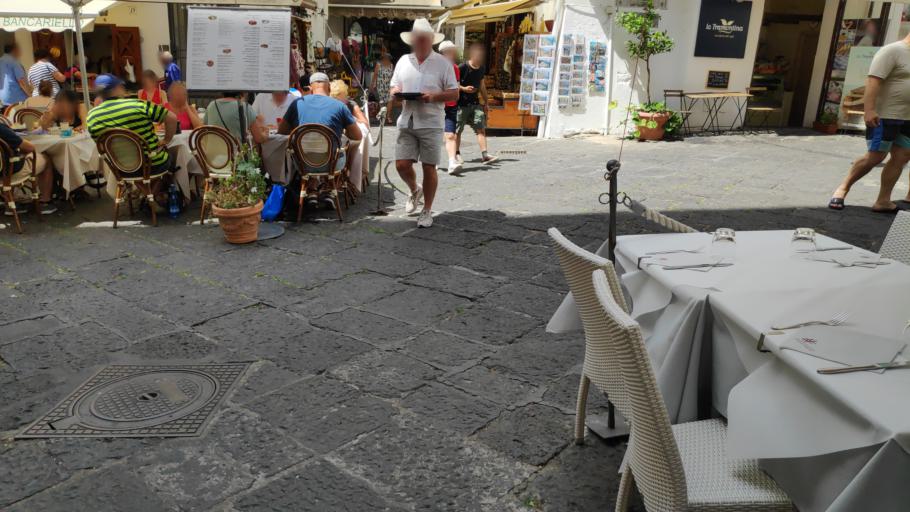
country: IT
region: Campania
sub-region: Provincia di Salerno
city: Amalfi
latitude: 40.6343
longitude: 14.6019
